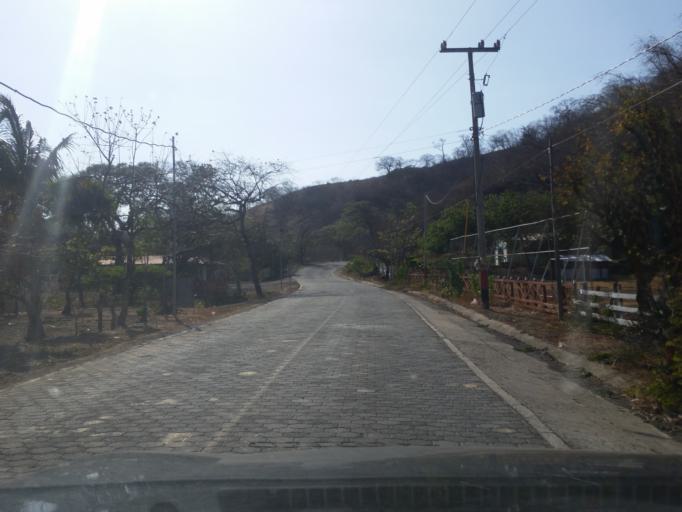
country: NI
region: Rivas
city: Tola
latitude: 11.3931
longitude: -85.9695
